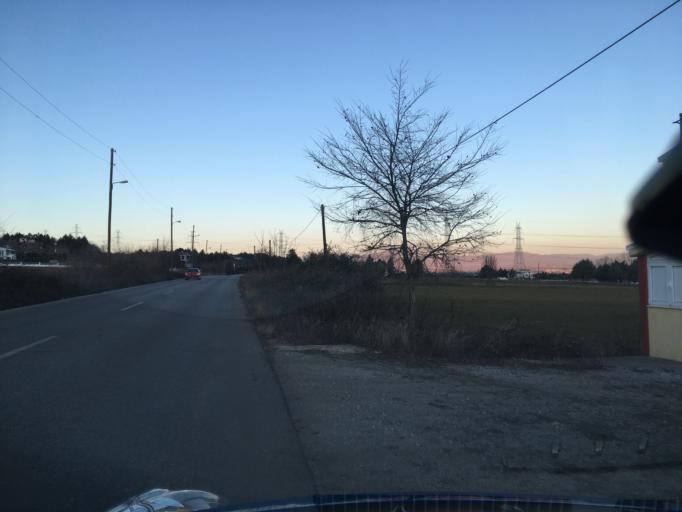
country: GR
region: West Macedonia
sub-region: Nomos Kozanis
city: Kozani
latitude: 40.2586
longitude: 21.7597
